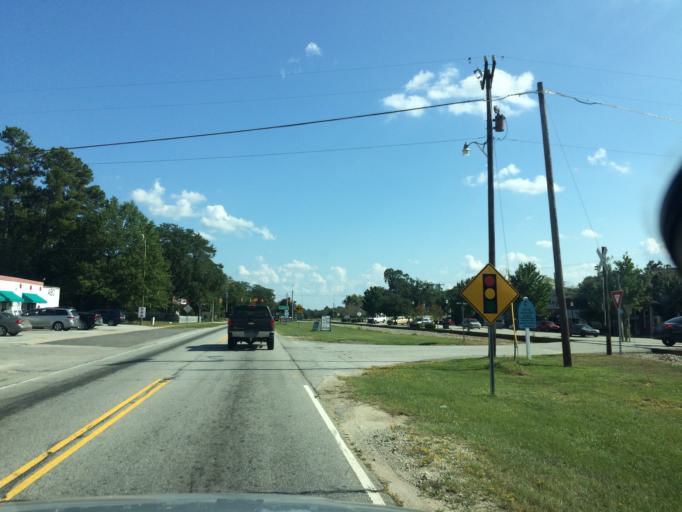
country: US
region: South Carolina
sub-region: Greenville County
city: Fountain Inn
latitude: 34.6087
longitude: -82.1142
